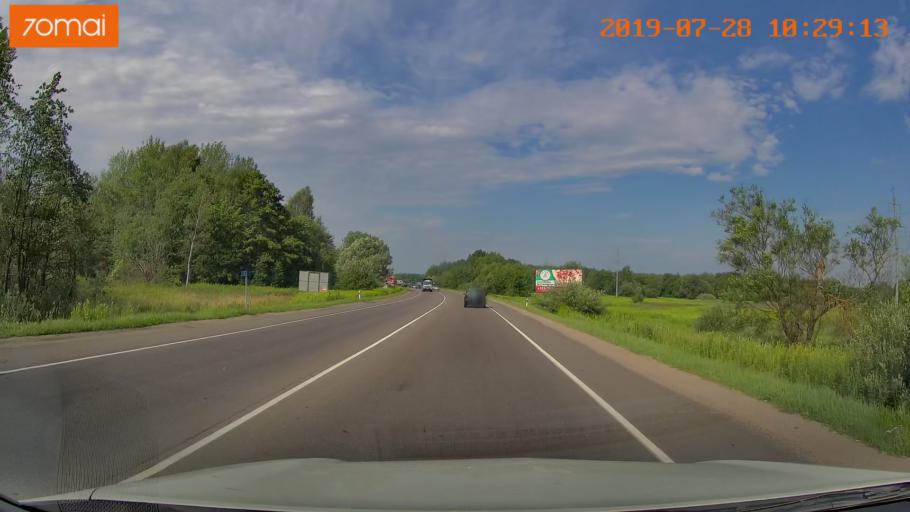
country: RU
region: Kaliningrad
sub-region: Gorod Kaliningrad
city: Kaliningrad
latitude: 54.7664
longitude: 20.4855
